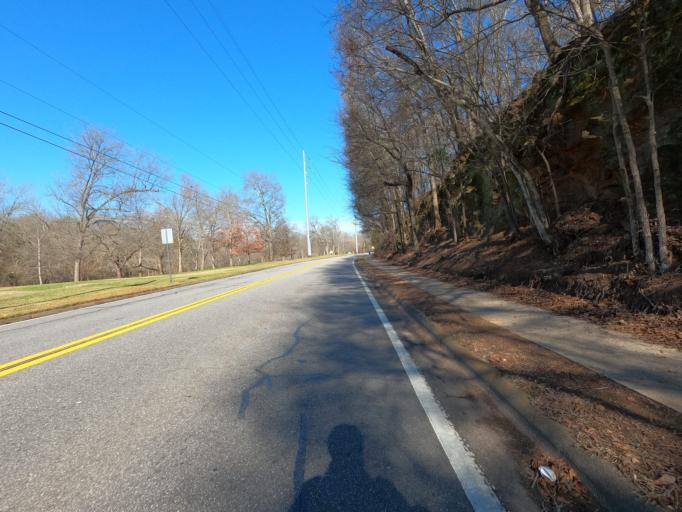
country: US
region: Georgia
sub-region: Clarke County
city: Athens
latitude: 33.9610
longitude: -83.3675
